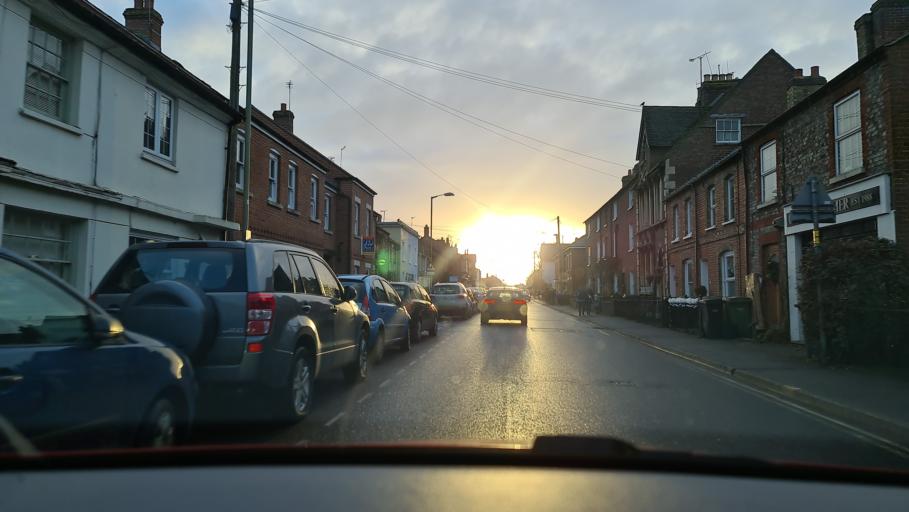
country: GB
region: England
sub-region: Oxfordshire
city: Thame
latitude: 51.7450
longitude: -0.9735
